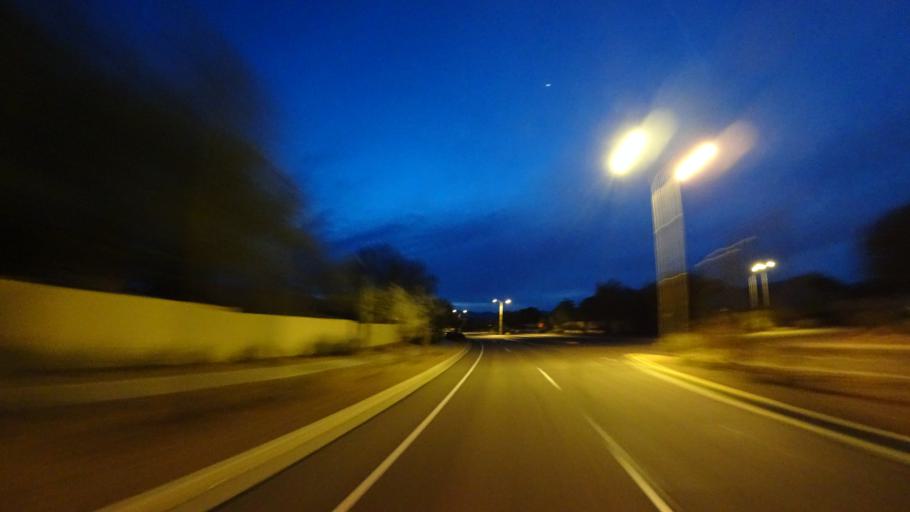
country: US
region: Arizona
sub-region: Maricopa County
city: Guadalupe
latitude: 33.3120
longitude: -112.0252
